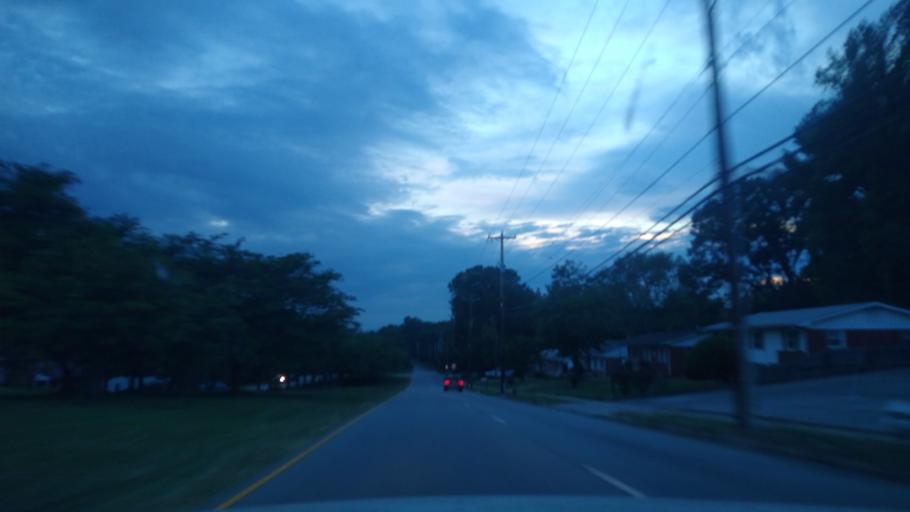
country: US
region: North Carolina
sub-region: Guilford County
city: Greensboro
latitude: 36.1135
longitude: -79.7679
